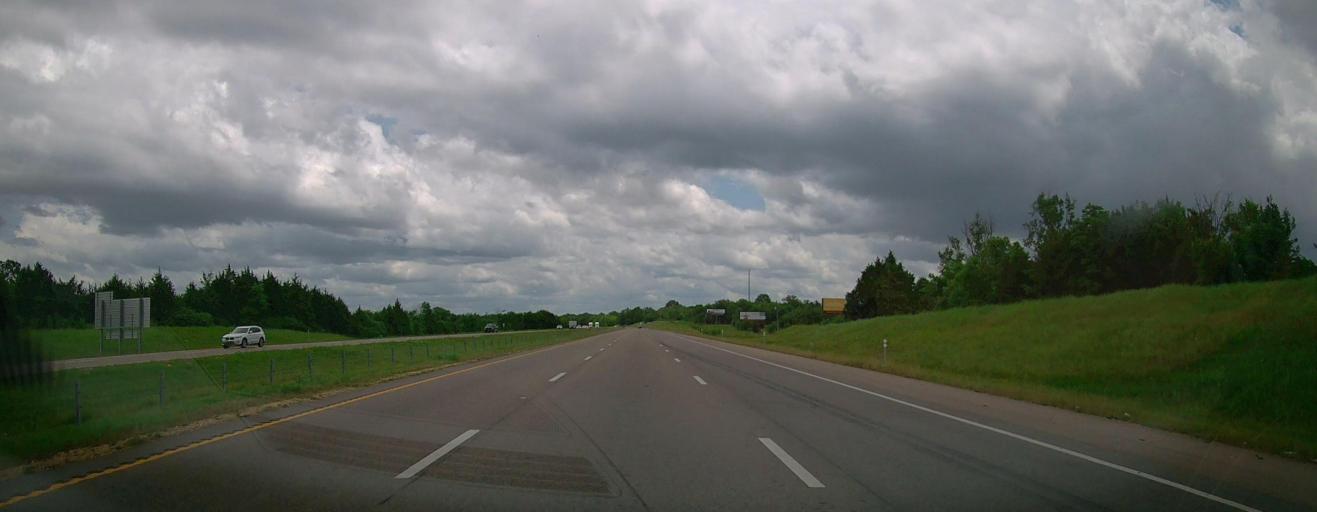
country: US
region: Mississippi
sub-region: Lee County
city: Tupelo
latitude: 34.3053
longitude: -88.7652
